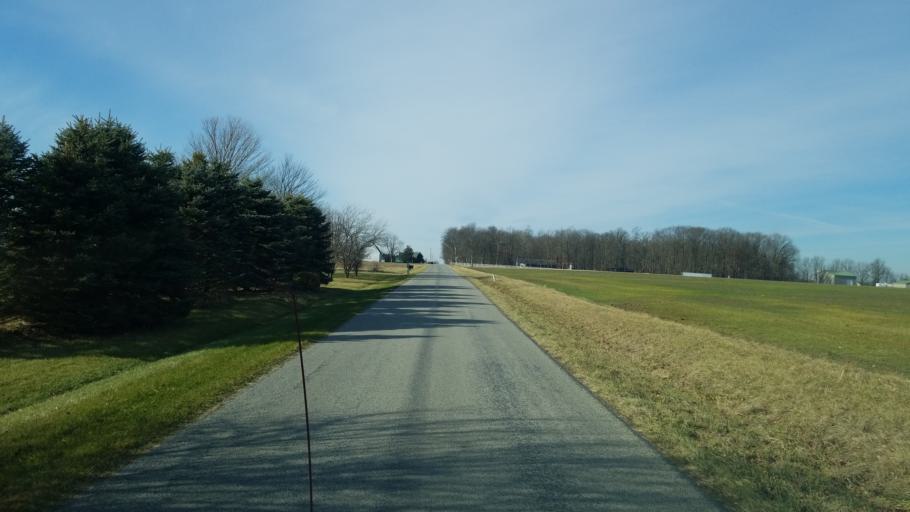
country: US
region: Ohio
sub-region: Allen County
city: Bluffton
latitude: 40.8123
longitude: -83.8953
